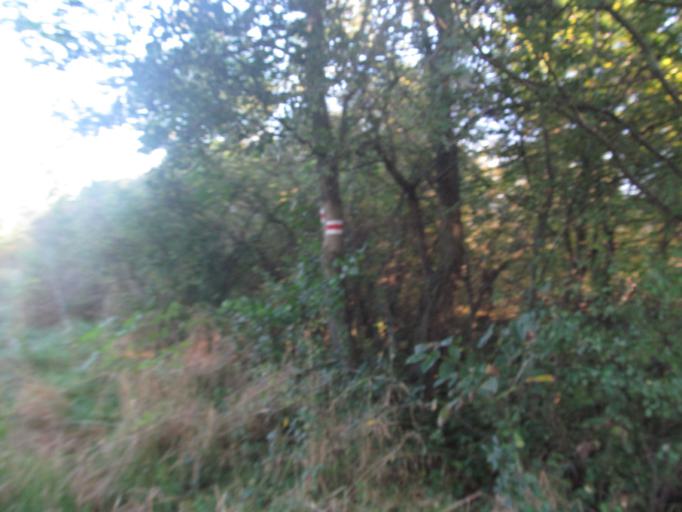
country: HU
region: Gyor-Moson-Sopron
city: Sopron
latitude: 47.7022
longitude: 16.5806
